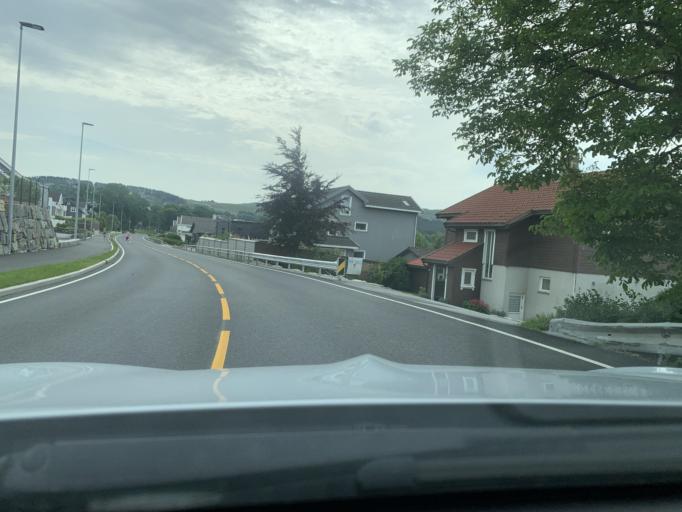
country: NO
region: Rogaland
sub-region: Sandnes
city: Sandnes
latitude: 58.7767
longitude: 5.7204
